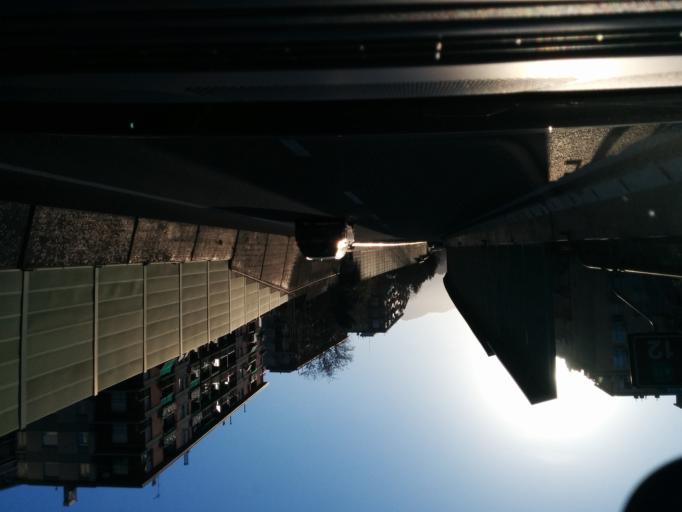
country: IT
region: Liguria
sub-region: Provincia di Genova
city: Mele
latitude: 44.4302
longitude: 8.7741
